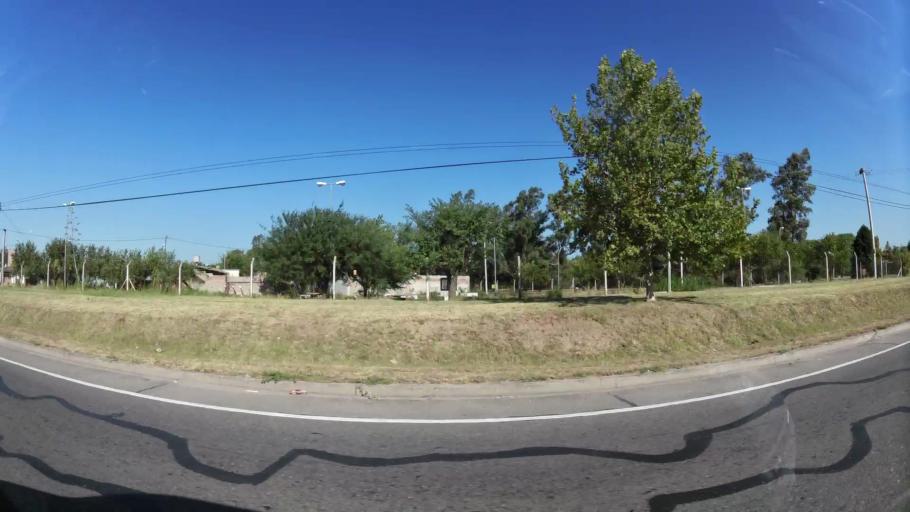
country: AR
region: Cordoba
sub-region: Departamento de Capital
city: Cordoba
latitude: -31.4839
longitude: -64.2441
